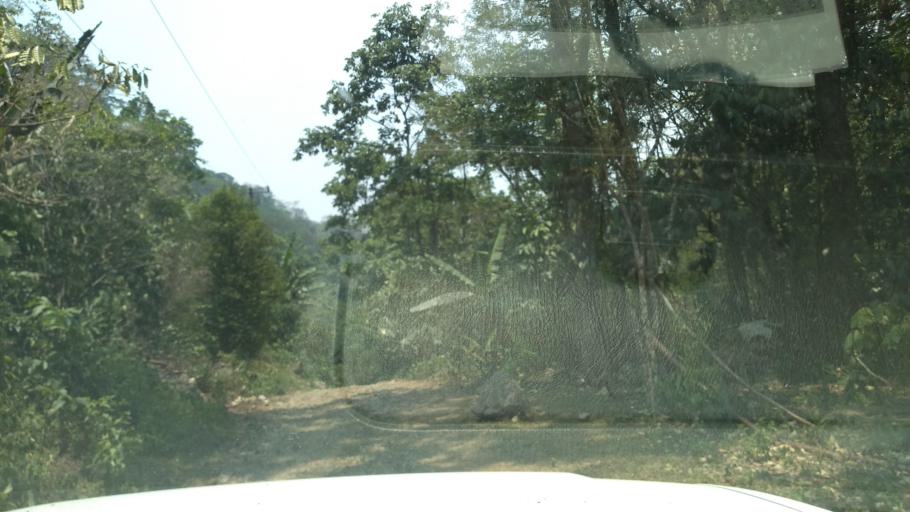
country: MX
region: Veracruz
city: Motzorongo
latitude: 18.5987
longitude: -96.7393
